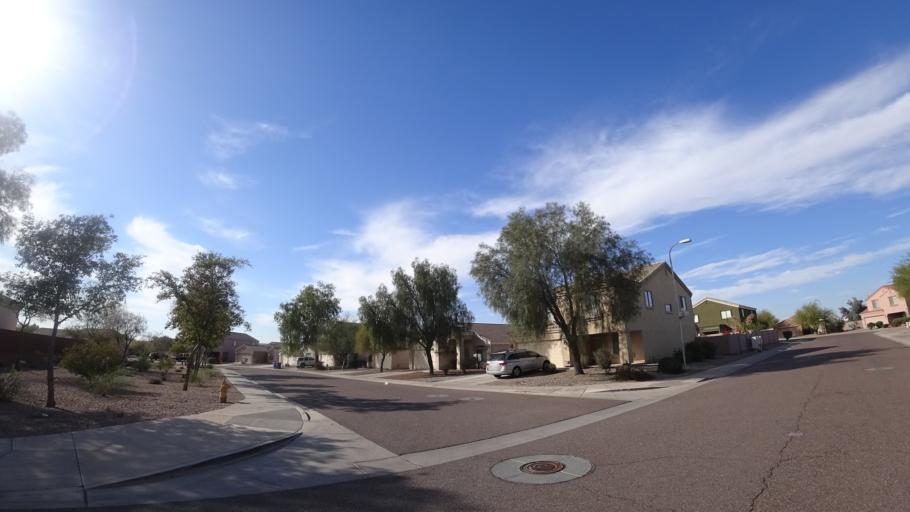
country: US
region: Arizona
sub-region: Maricopa County
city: Tolleson
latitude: 33.4320
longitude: -112.2859
